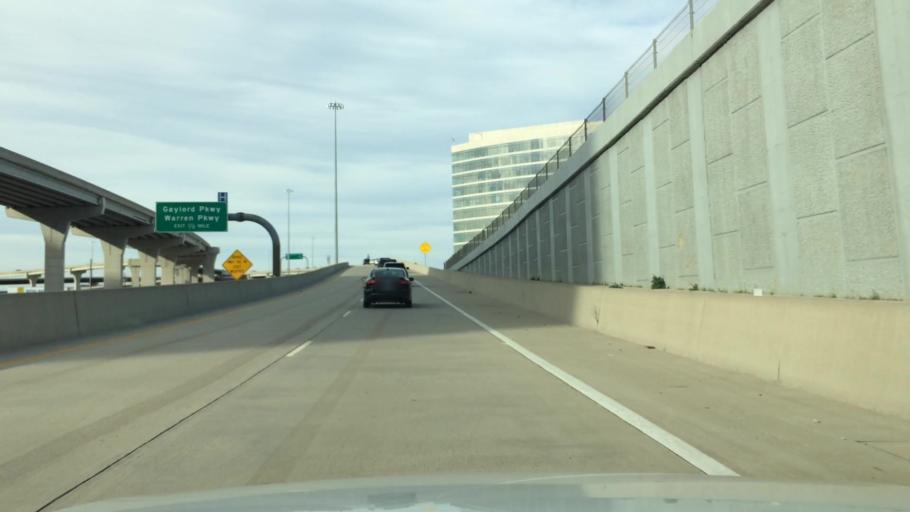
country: US
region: Texas
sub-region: Denton County
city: The Colony
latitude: 33.0848
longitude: -96.8236
